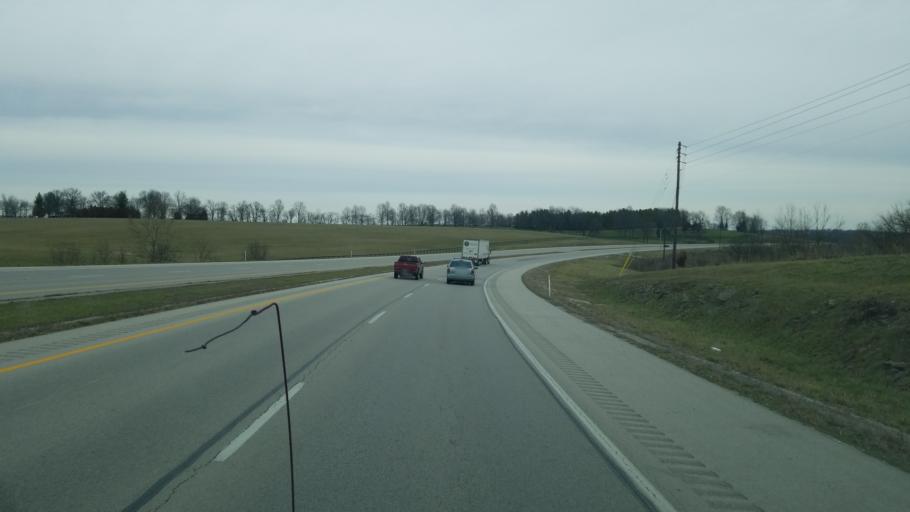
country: US
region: Kentucky
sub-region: Bourbon County
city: Paris
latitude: 38.2245
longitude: -84.2740
